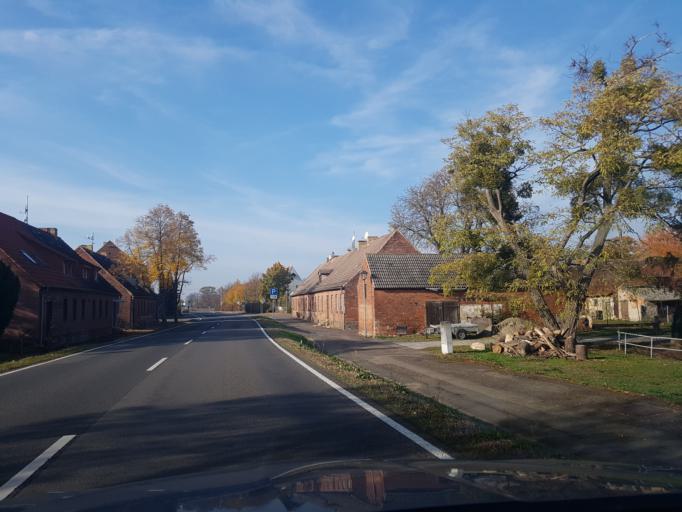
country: DE
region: Saxony
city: Beilrode
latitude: 51.5433
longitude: 13.0613
